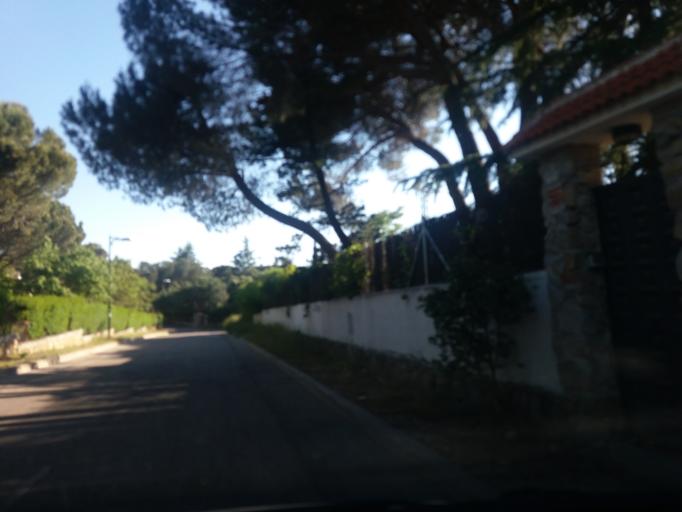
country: ES
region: Madrid
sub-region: Provincia de Madrid
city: Torrelodones
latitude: 40.5838
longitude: -3.9587
